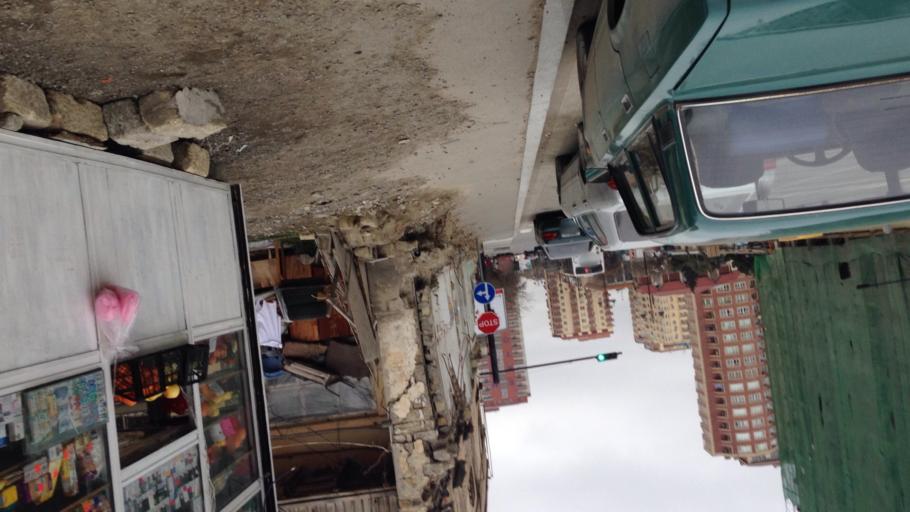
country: AZ
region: Baki
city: Baku
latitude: 40.3984
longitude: 49.8430
